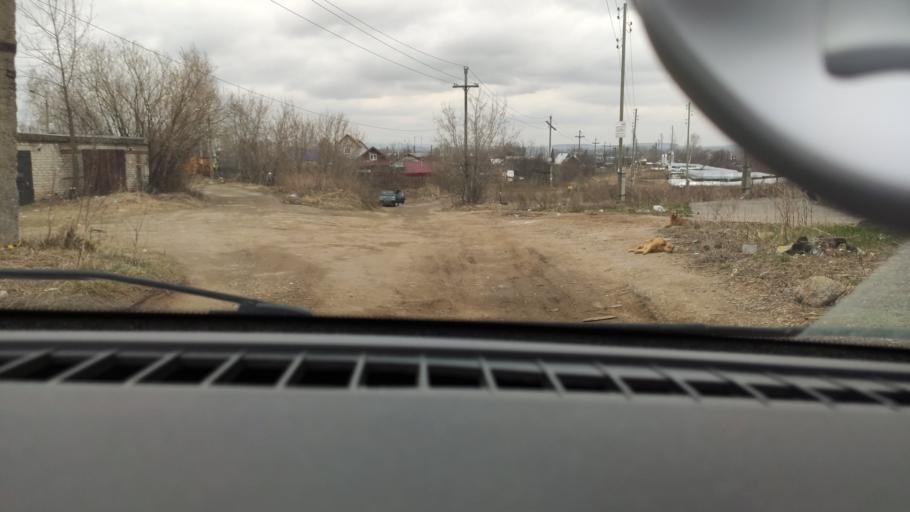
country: RU
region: Perm
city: Kondratovo
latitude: 57.9590
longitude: 56.1465
